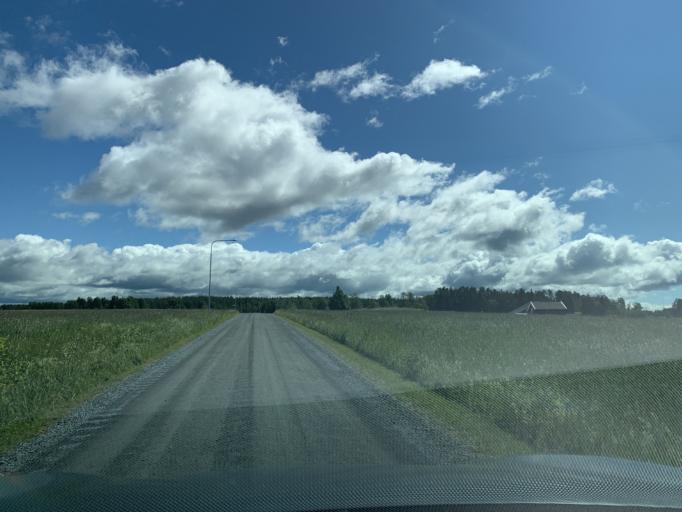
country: SE
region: Jaemtland
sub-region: Krokoms Kommun
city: Krokom
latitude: 63.1478
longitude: 14.3440
